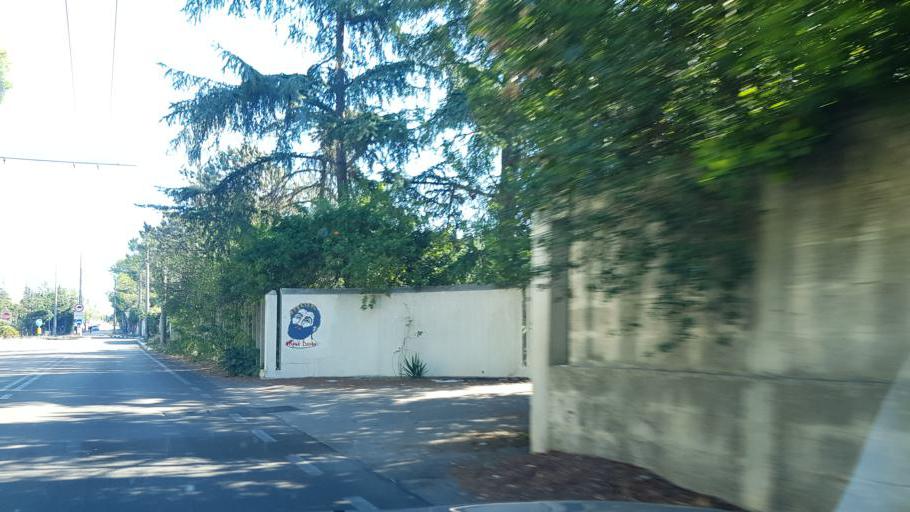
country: IT
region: Apulia
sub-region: Provincia di Lecce
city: San Pietro in Lama
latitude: 40.3394
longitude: 18.1351
